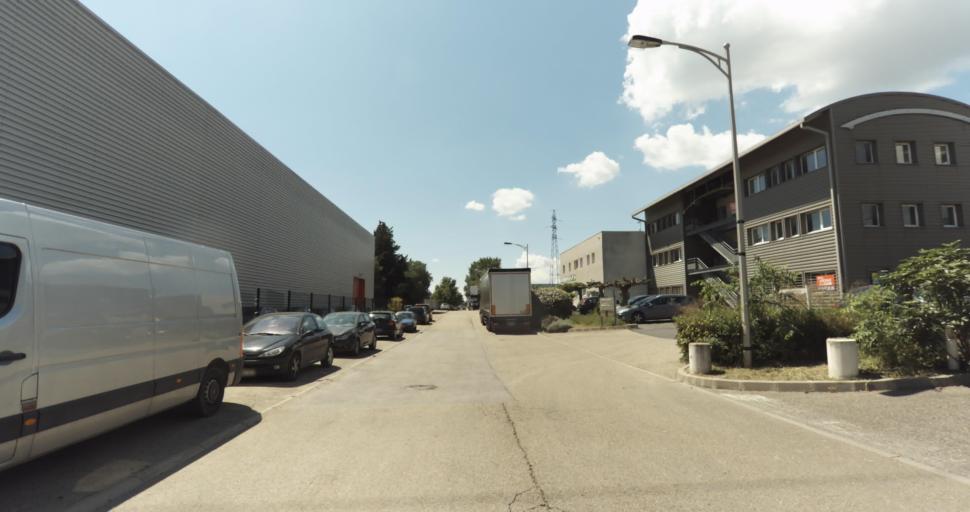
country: FR
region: Languedoc-Roussillon
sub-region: Departement du Gard
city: Nimes
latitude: 43.8103
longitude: 4.3384
